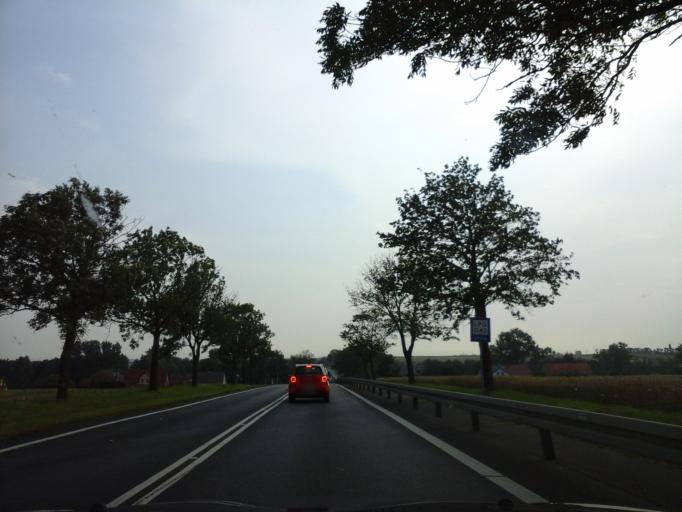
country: PL
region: Greater Poland Voivodeship
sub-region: Powiat koscianski
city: Koscian
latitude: 52.0598
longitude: 16.5936
